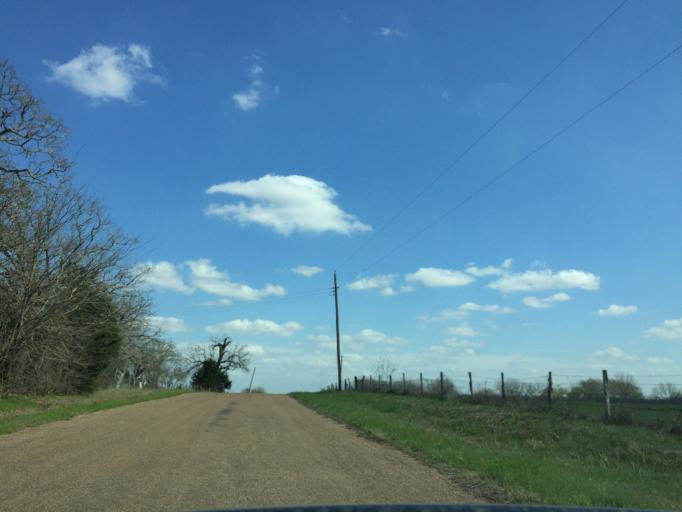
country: US
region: Texas
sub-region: Milam County
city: Thorndale
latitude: 30.5517
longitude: -97.1487
